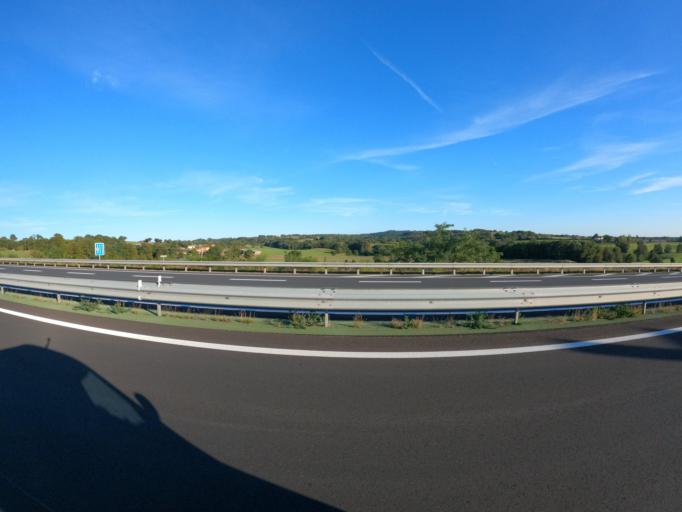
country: FR
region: Pays de la Loire
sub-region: Departement de la Vendee
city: La Gaubretiere
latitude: 46.9149
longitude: -1.0421
